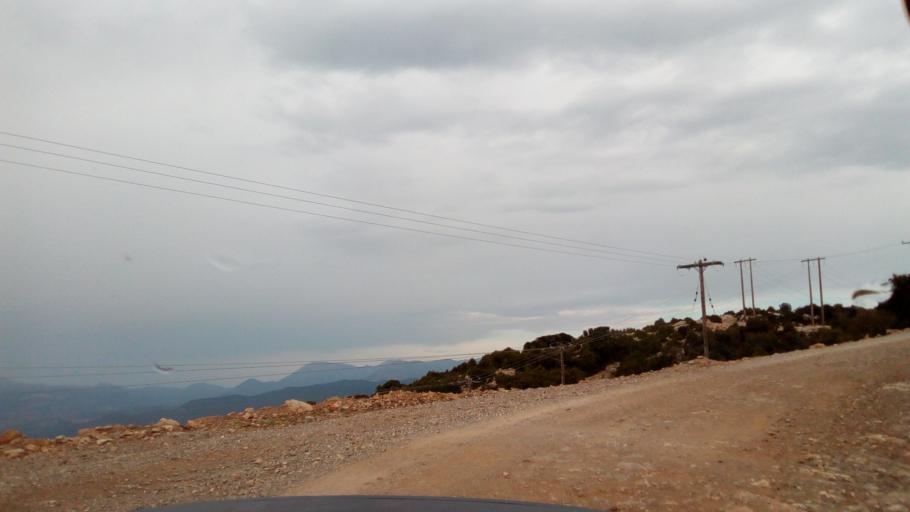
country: GR
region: West Greece
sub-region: Nomos Achaias
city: Kamarai
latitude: 38.4181
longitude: 22.0393
